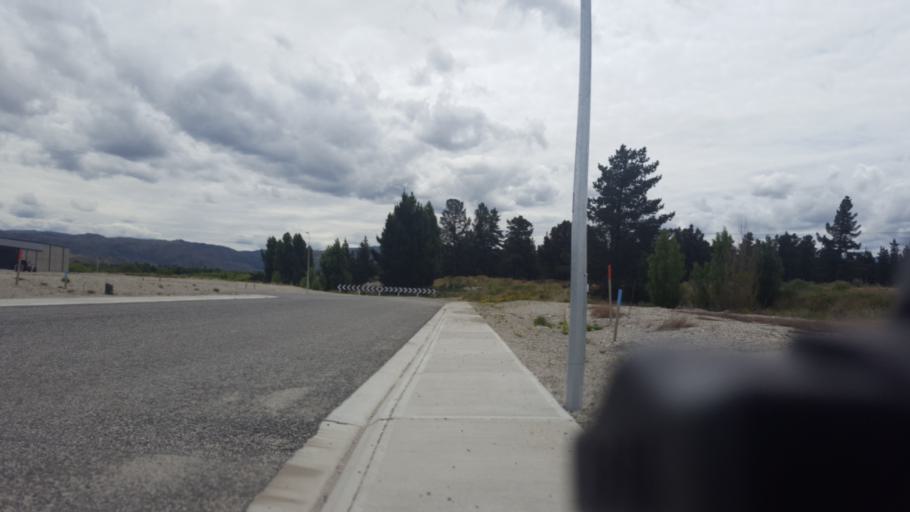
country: NZ
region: Otago
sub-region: Queenstown-Lakes District
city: Wanaka
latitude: -45.2465
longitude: 169.3717
